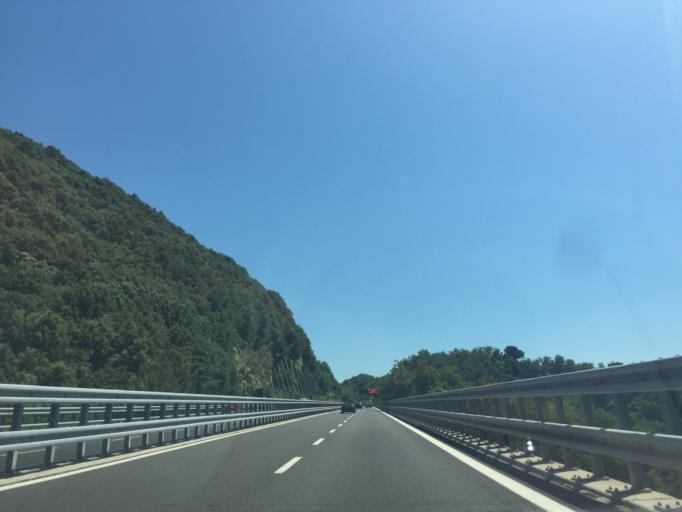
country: IT
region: Tuscany
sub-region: Provincia di Lucca
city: Massarosa
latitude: 43.8648
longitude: 10.3664
